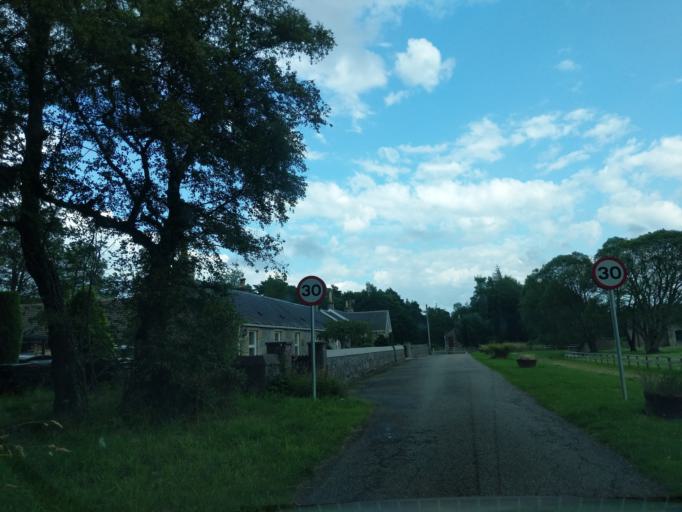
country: GB
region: Scotland
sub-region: Moray
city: Rothes
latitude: 57.4554
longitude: -3.3012
